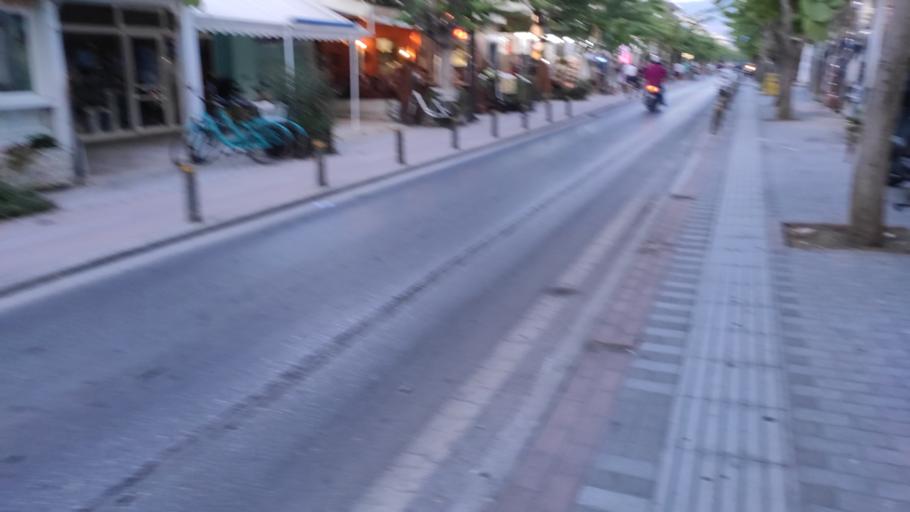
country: GR
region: South Aegean
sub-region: Nomos Dodekanisou
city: Kos
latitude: 36.9000
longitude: 27.2833
